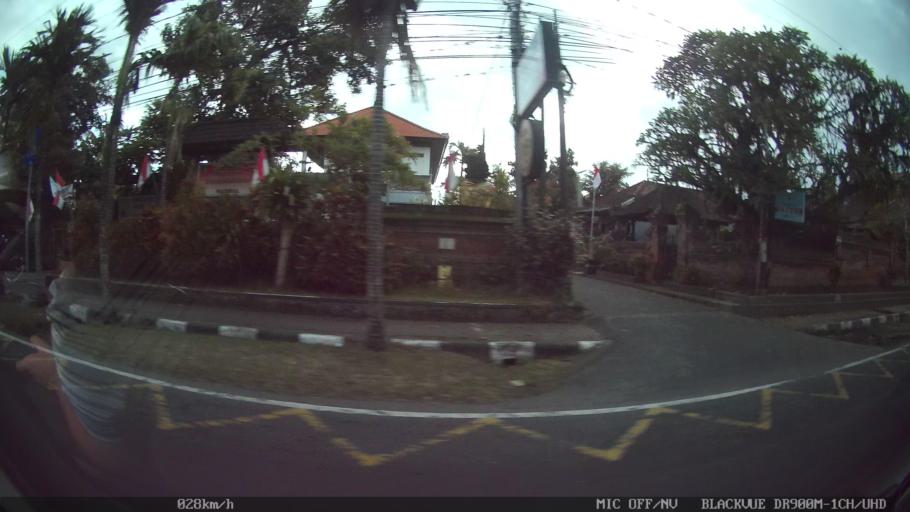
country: ID
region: Bali
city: Banjar Mambalkajanan
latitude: -8.5522
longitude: 115.2194
